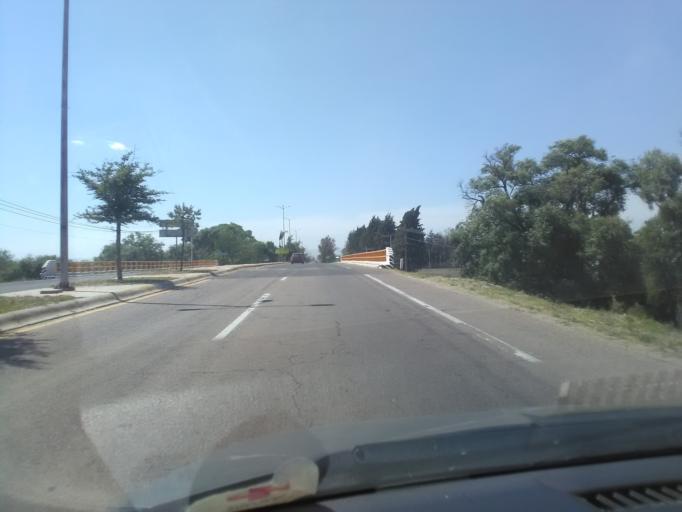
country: MX
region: Durango
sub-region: Durango
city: Jose Refugio Salcido
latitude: 24.0253
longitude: -104.5639
